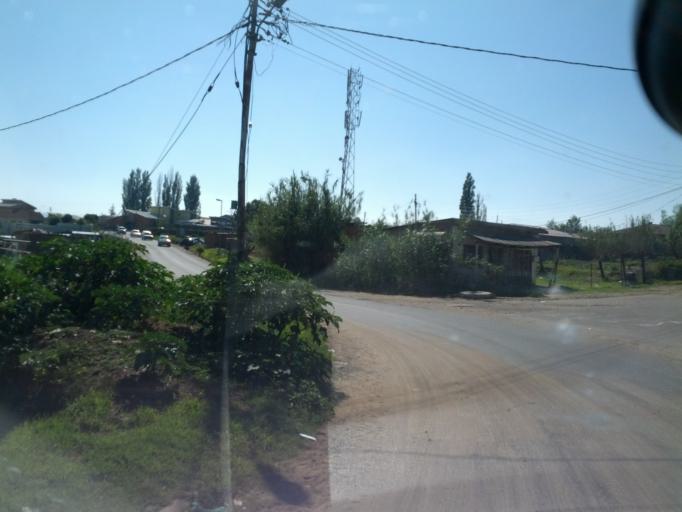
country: LS
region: Maseru
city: Maseru
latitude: -29.3074
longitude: 27.4961
